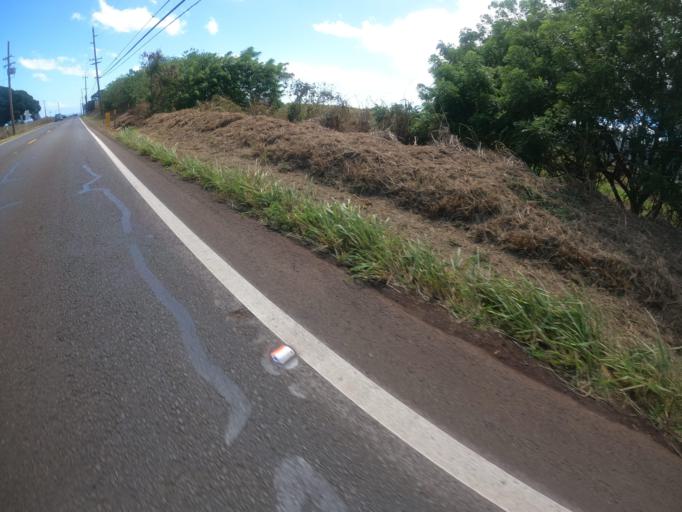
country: US
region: Hawaii
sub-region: Honolulu County
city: Village Park
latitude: 21.4209
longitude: -158.0503
